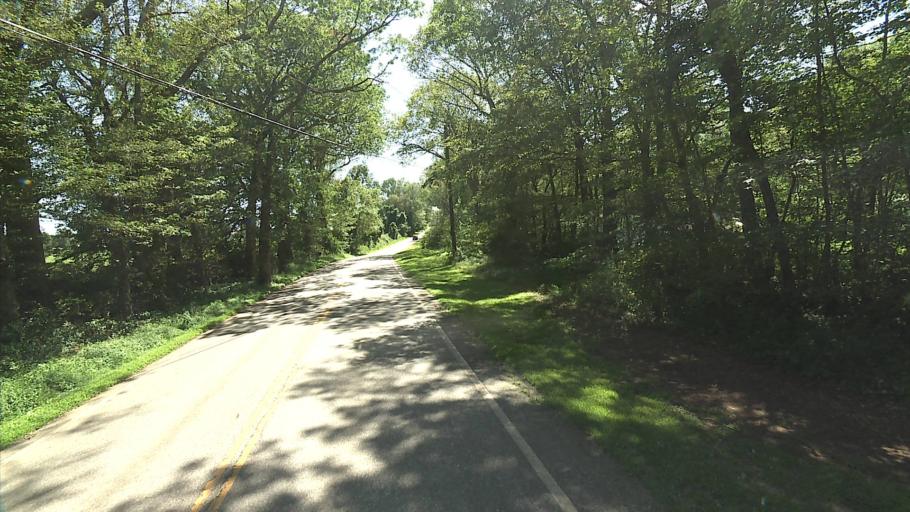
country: US
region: Connecticut
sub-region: New London County
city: Baltic
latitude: 41.7025
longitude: -72.0683
